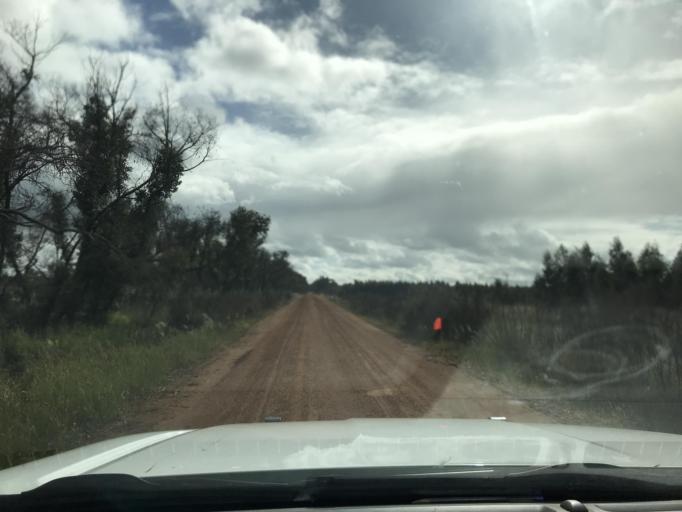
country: AU
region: South Australia
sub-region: Wattle Range
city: Penola
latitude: -37.1894
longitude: 141.1876
